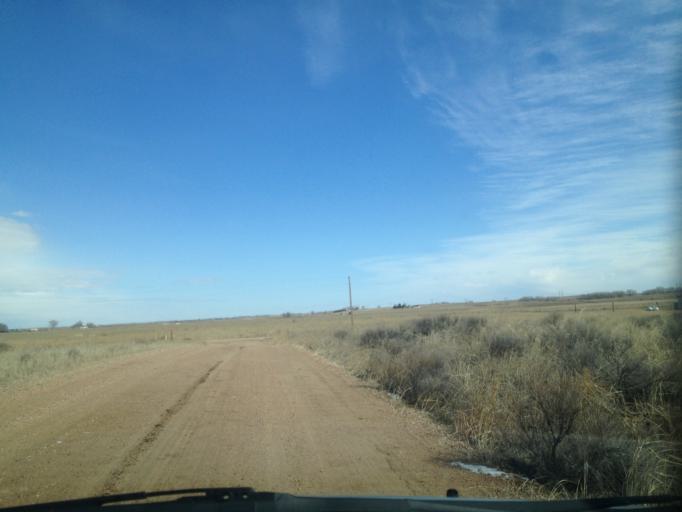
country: US
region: Colorado
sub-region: Weld County
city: Keenesburg
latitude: 40.2873
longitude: -104.2567
